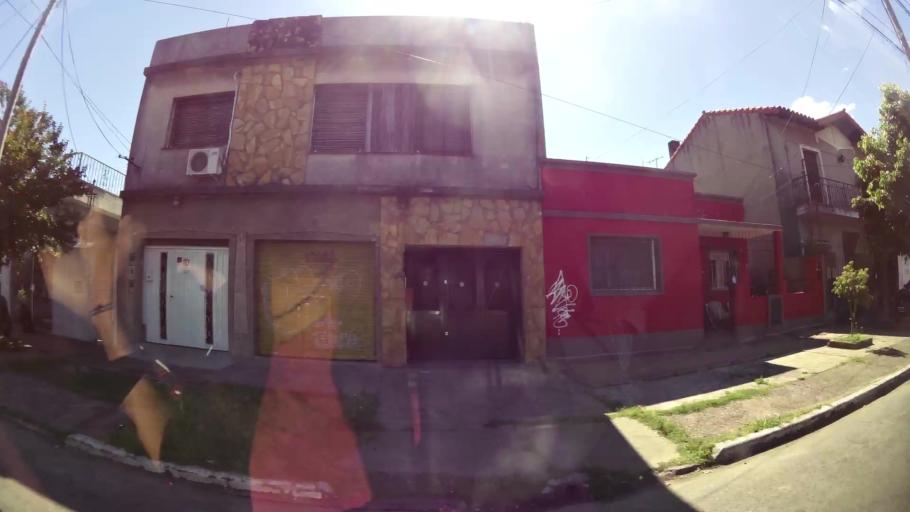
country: AR
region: Buenos Aires
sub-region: Partido de Lomas de Zamora
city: Lomas de Zamora
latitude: -34.7583
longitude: -58.4218
